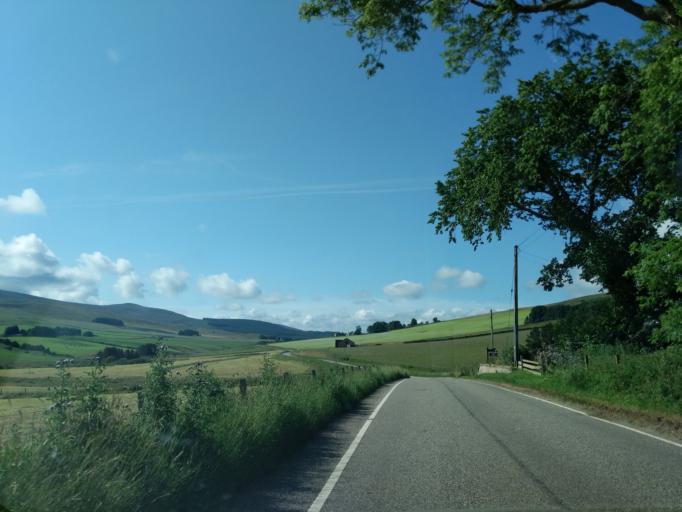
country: GB
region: Scotland
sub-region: Moray
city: Dufftown
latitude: 57.3870
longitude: -3.2178
